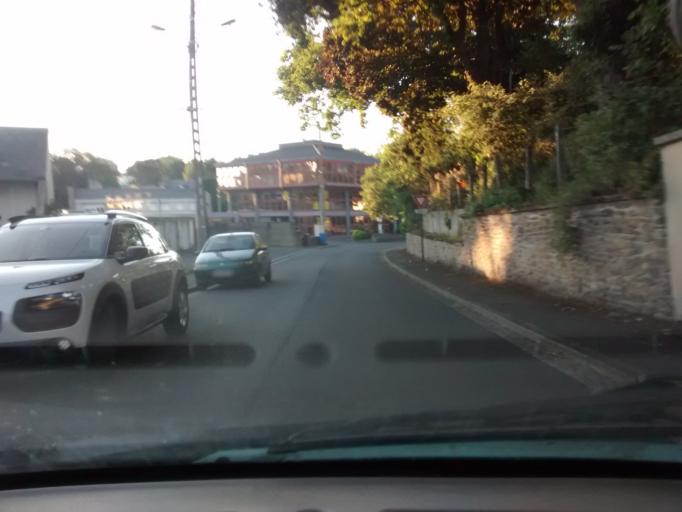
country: FR
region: Lower Normandy
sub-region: Departement de la Manche
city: Saint-Lo
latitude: 49.1124
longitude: -1.0810
